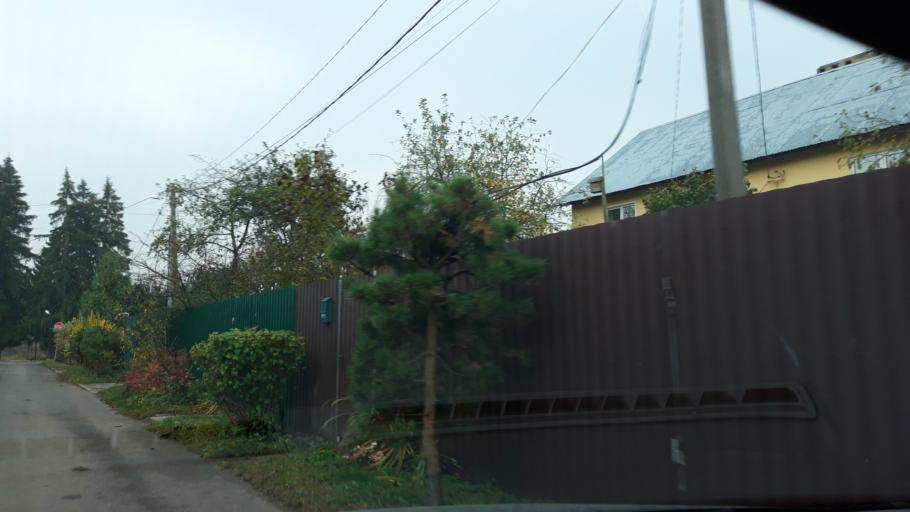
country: RU
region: Moskovskaya
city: Chashnikovo
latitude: 56.0209
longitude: 37.1833
